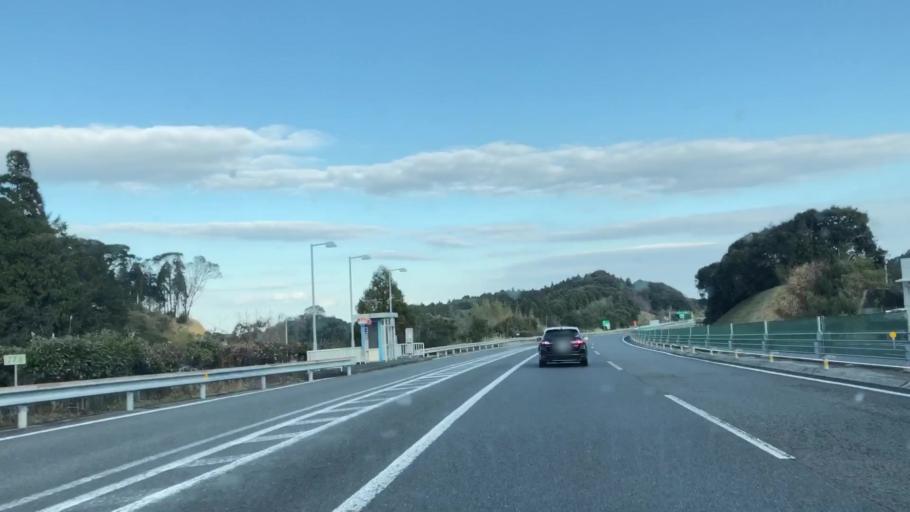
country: JP
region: Miyazaki
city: Miyazaki-shi
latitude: 31.8666
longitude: 131.3884
